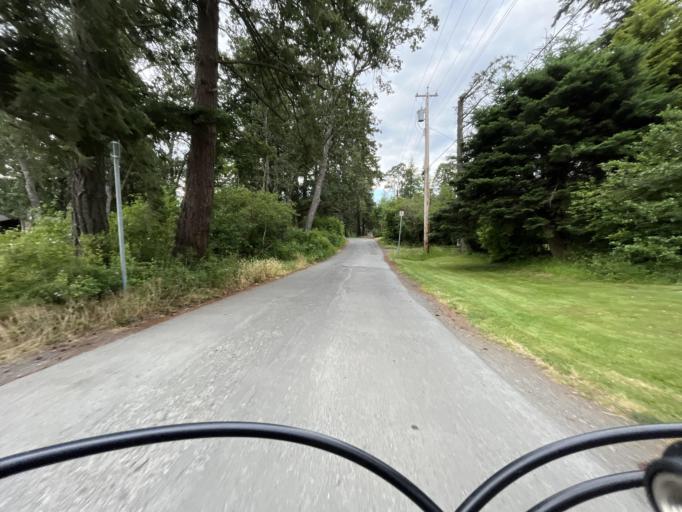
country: CA
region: British Columbia
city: Oak Bay
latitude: 48.4790
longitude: -123.3453
